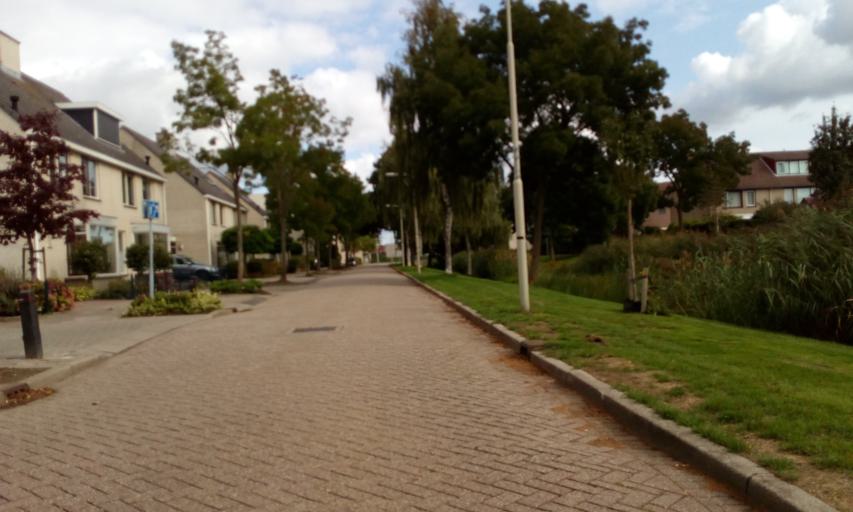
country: NL
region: South Holland
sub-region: Gemeente Lansingerland
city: Bleiswijk
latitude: 52.0117
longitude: 4.5456
